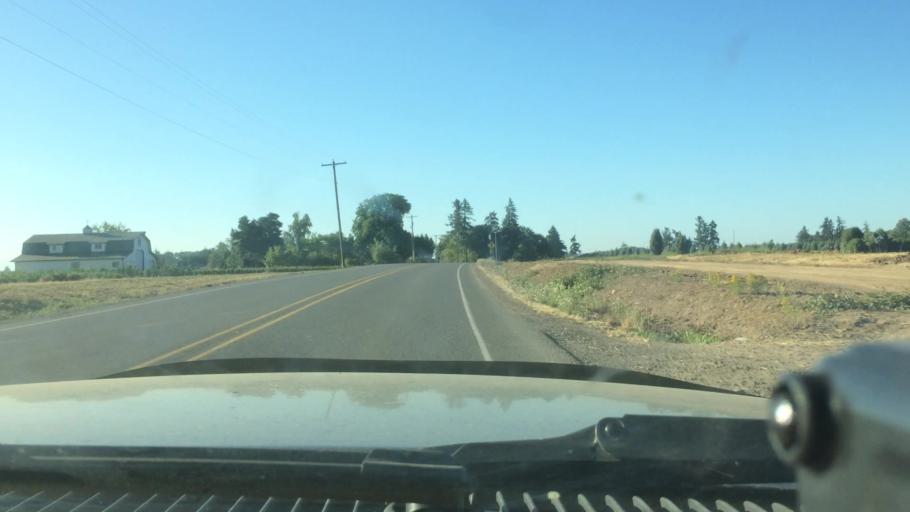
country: US
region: Oregon
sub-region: Marion County
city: Gervais
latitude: 45.1224
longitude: -122.9861
